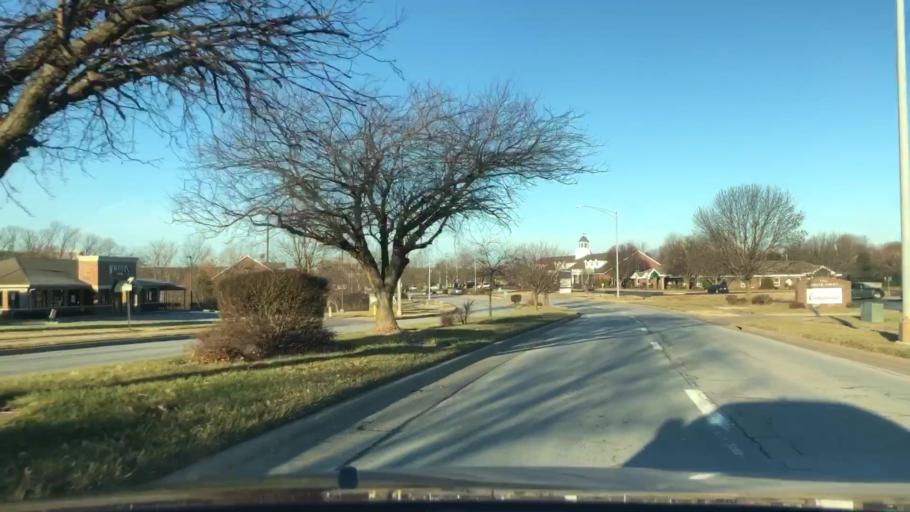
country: US
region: Missouri
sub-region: Greene County
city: Springfield
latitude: 37.1473
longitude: -93.2690
